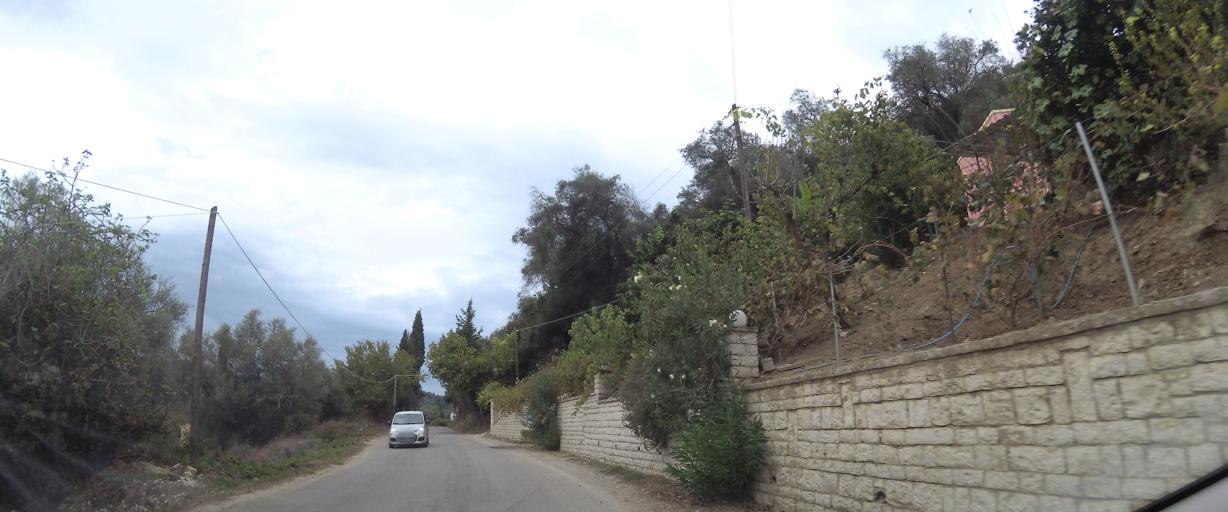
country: GR
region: Ionian Islands
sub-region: Nomos Kerkyras
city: Agios Georgis
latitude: 39.7534
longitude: 19.6863
